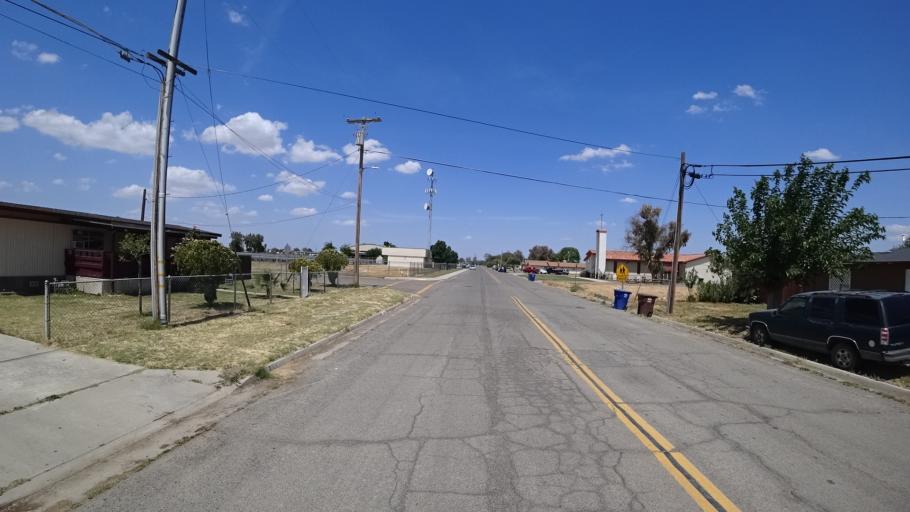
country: US
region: California
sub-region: Kings County
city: Stratford
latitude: 36.1904
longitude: -119.8206
